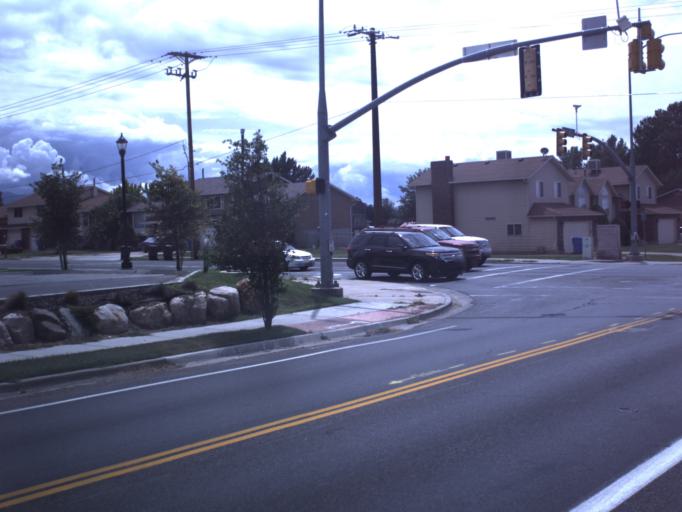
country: US
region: Utah
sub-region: Davis County
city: West Point
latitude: 41.1184
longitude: -112.0646
